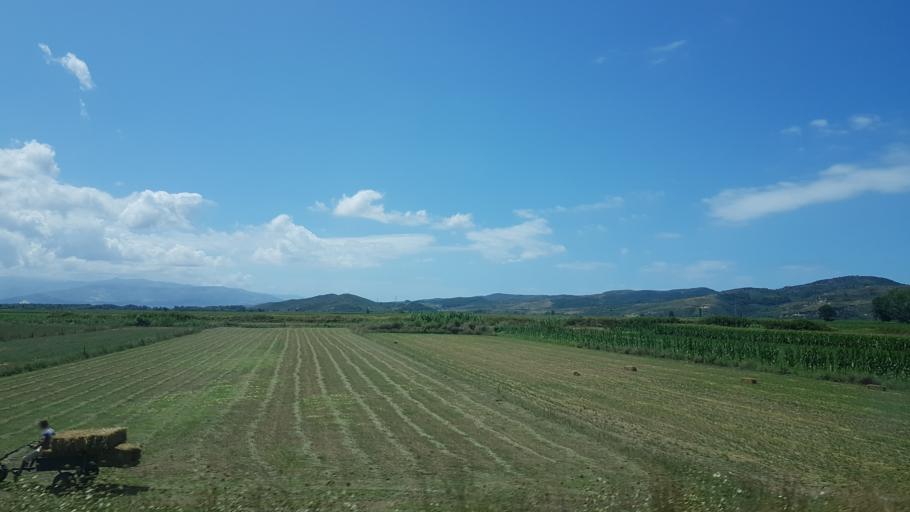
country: AL
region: Fier
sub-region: Rrethi i Fierit
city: Cakran
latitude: 40.6019
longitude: 19.5588
